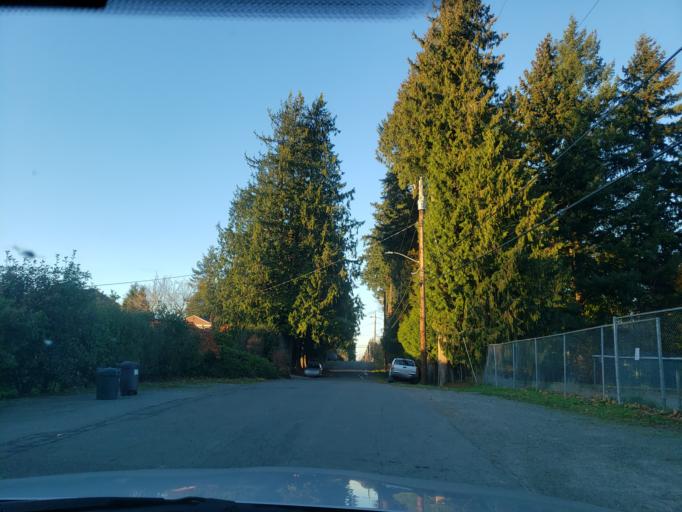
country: US
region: Washington
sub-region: Snohomish County
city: Esperance
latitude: 47.7981
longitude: -122.3642
